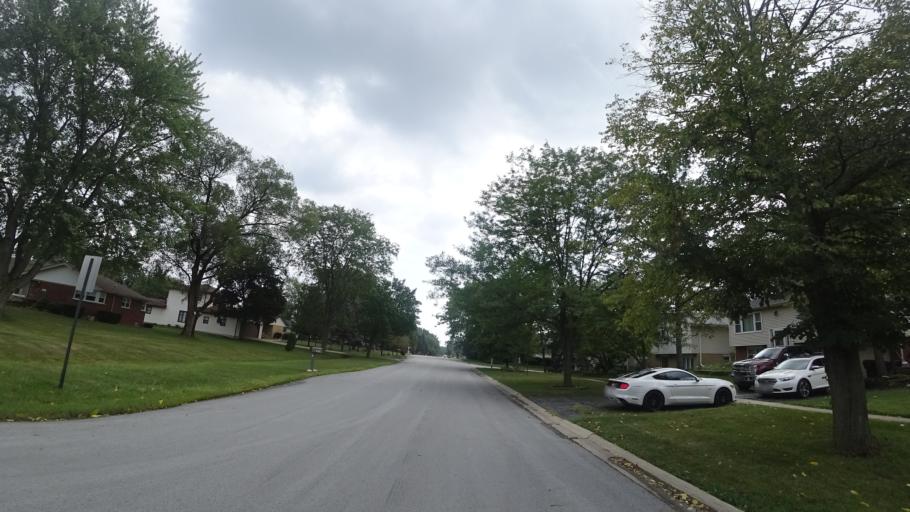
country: US
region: Illinois
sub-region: Cook County
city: Tinley Park
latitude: 41.5926
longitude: -87.7752
